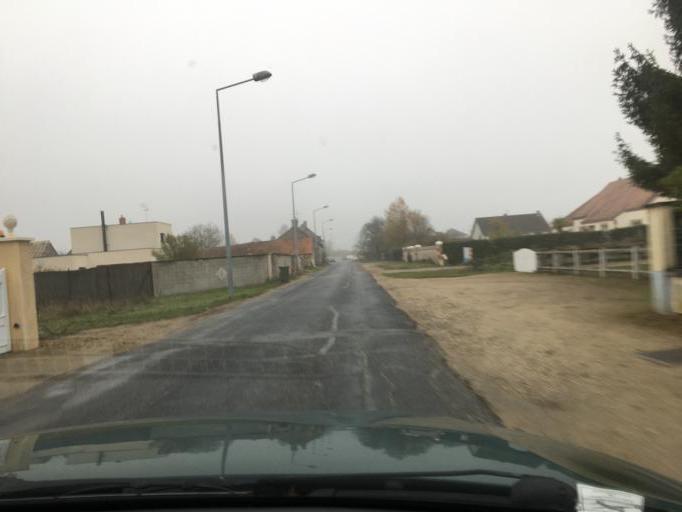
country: FR
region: Centre
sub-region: Departement du Loiret
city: Olivet
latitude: 47.8538
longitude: 1.9011
